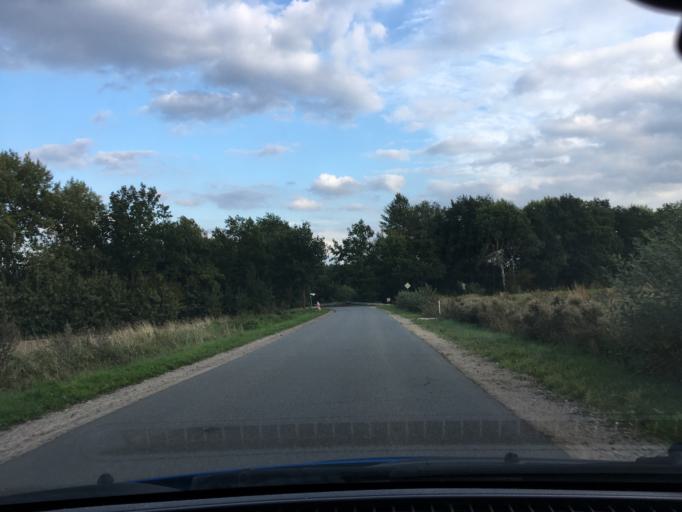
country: DE
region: Lower Saxony
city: Garstedt
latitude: 53.2807
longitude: 10.1798
